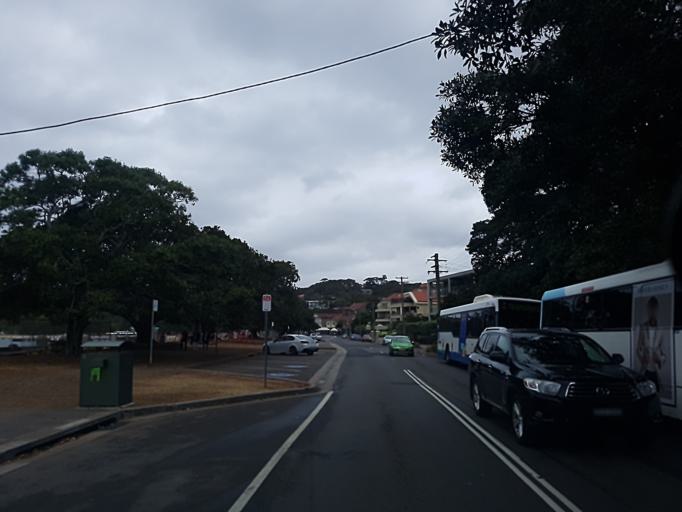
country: AU
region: New South Wales
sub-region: Manly Vale
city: Clontarf
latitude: -33.8244
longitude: 151.2509
